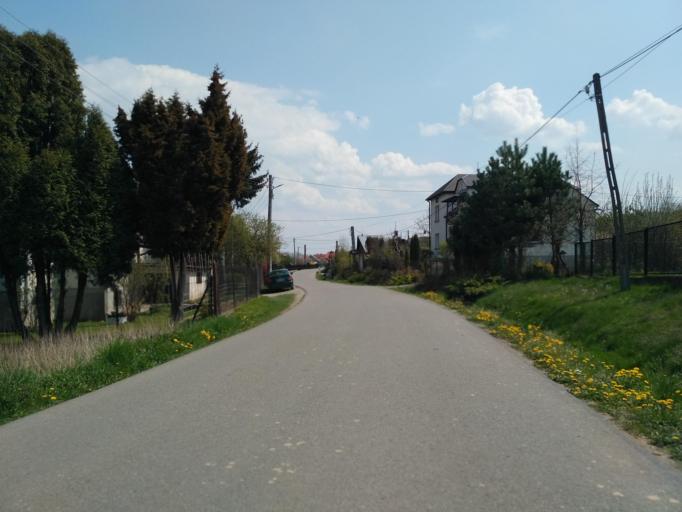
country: PL
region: Subcarpathian Voivodeship
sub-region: Powiat jasielski
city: Tarnowiec
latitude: 49.7337
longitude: 21.6087
